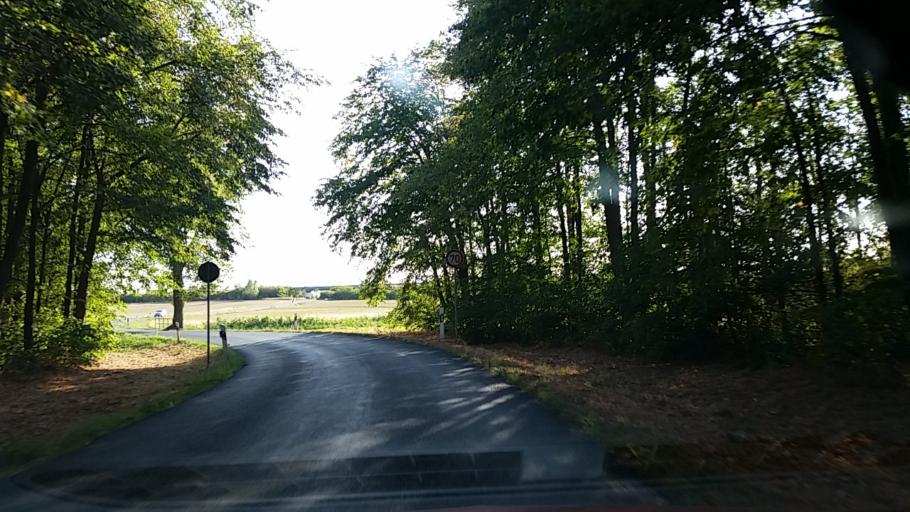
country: DE
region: Lower Saxony
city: Lehre
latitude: 52.3379
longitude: 10.6918
